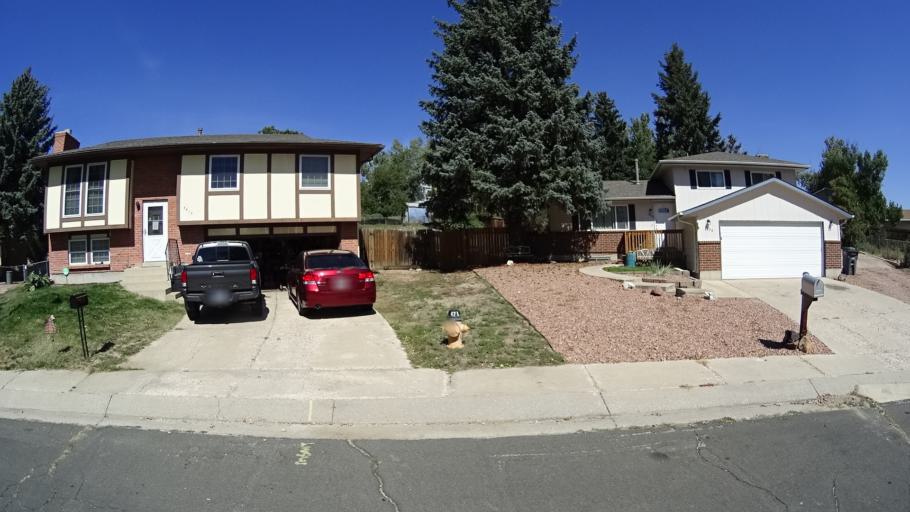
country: US
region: Colorado
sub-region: El Paso County
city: Cimarron Hills
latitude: 38.9079
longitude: -104.7644
